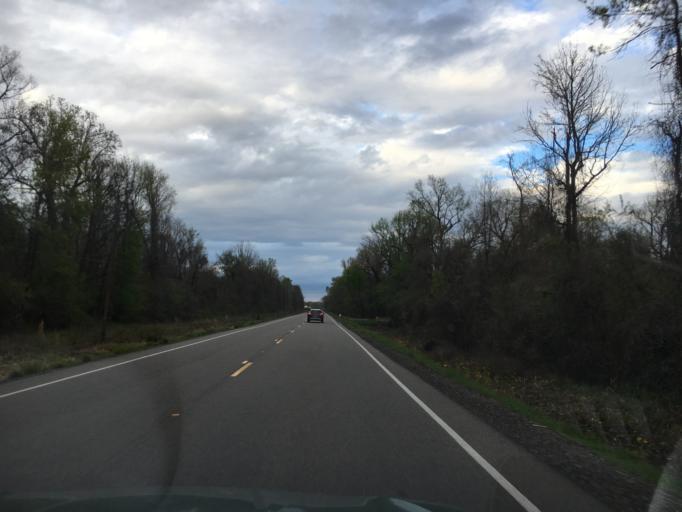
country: US
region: Louisiana
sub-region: West Baton Rouge Parish
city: Erwinville
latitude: 30.4719
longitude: -91.3990
